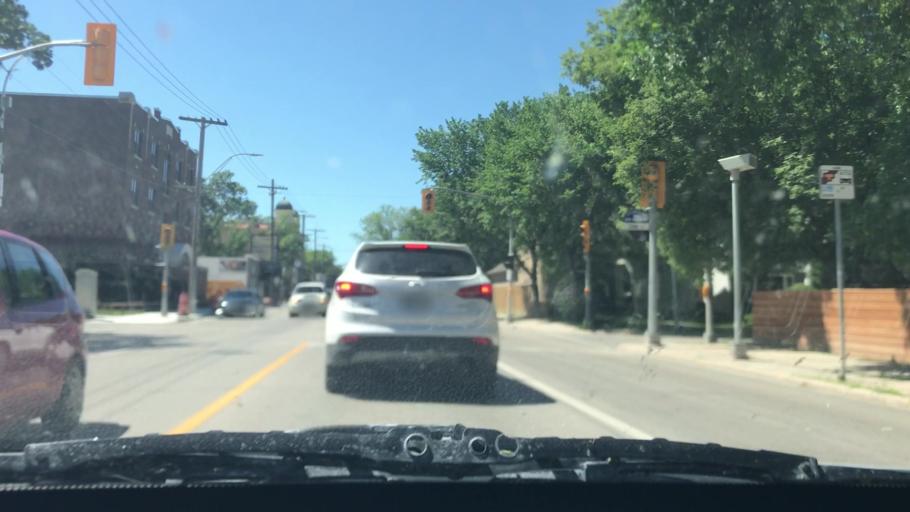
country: CA
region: Manitoba
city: Winnipeg
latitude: 49.8737
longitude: -97.1806
